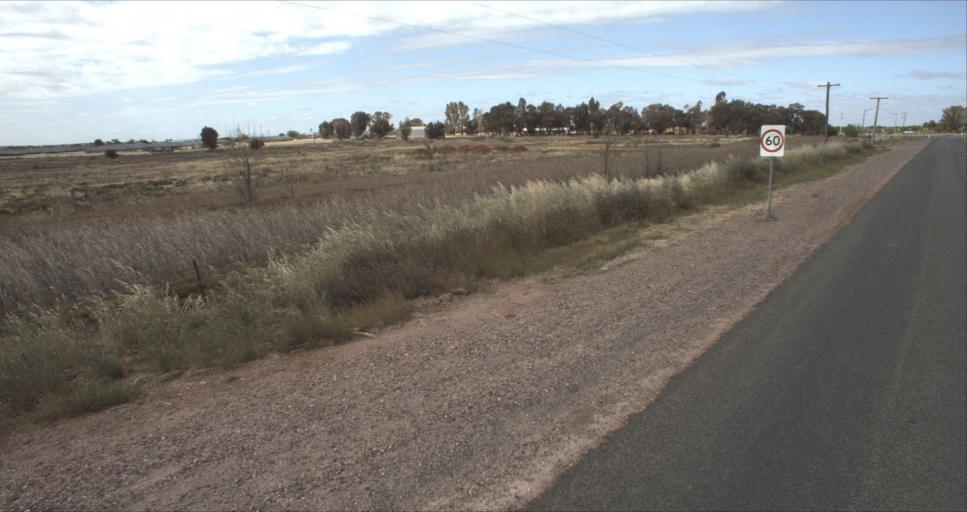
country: AU
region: New South Wales
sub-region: Leeton
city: Leeton
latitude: -34.5673
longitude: 146.3960
